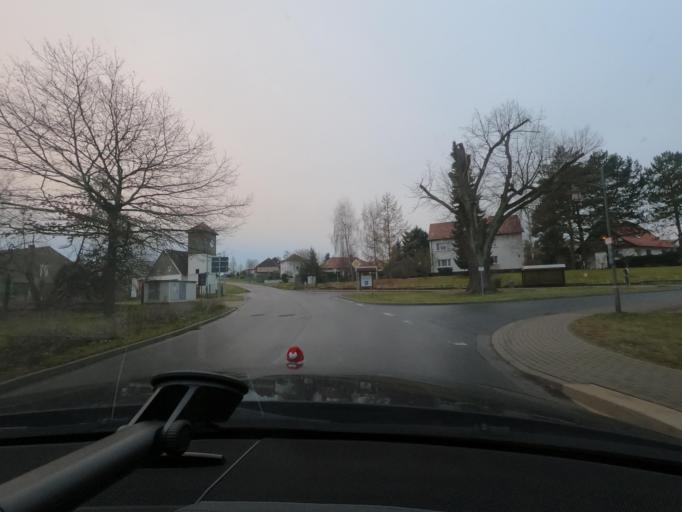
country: DE
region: Thuringia
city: Helmsdorf
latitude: 51.2776
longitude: 10.4047
